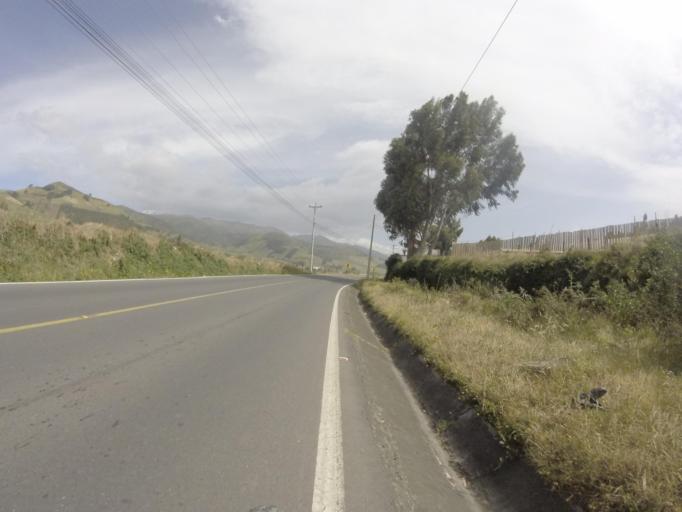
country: EC
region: Pichincha
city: Cayambe
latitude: 0.1215
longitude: -78.0860
